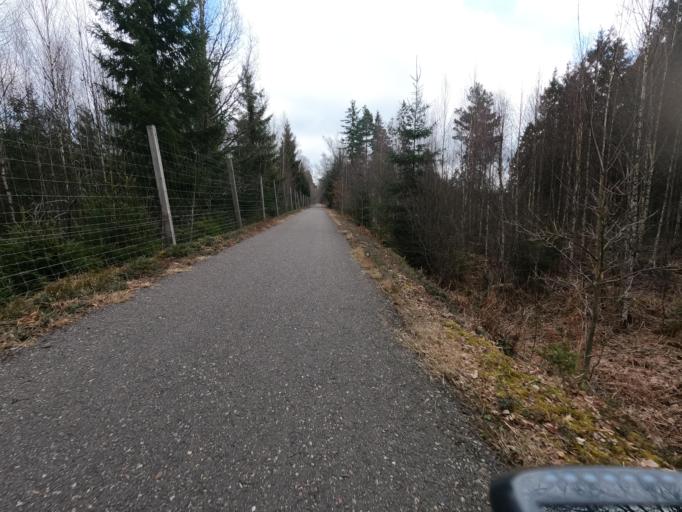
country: SE
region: Joenkoeping
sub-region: Varnamo Kommun
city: Rydaholm
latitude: 56.8562
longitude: 14.1835
